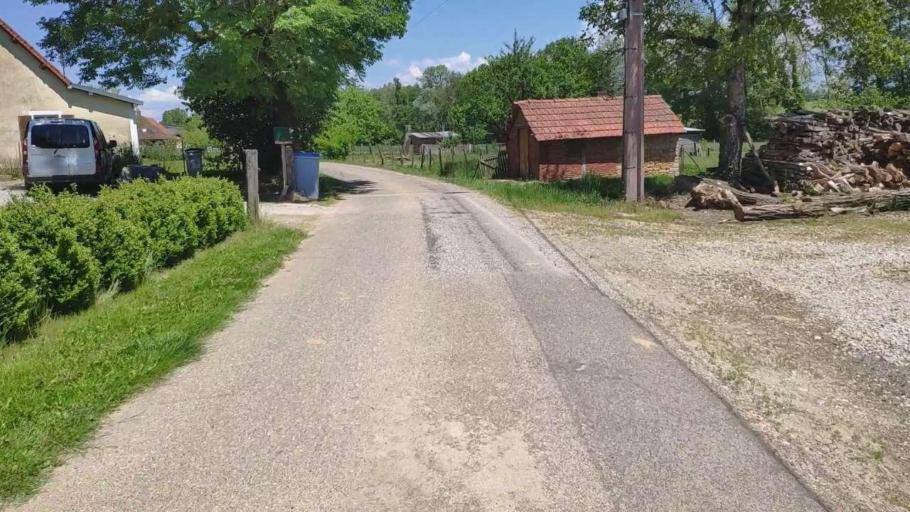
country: FR
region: Franche-Comte
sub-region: Departement du Jura
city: Bletterans
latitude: 46.7486
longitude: 5.4069
